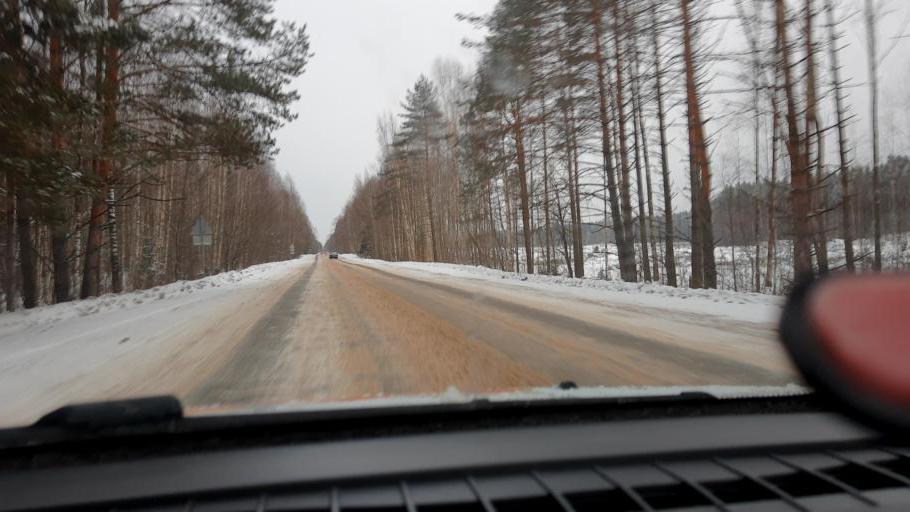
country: RU
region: Nizjnij Novgorod
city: Pamyat' Parizhskoy Kommuny
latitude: 56.2775
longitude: 44.3903
